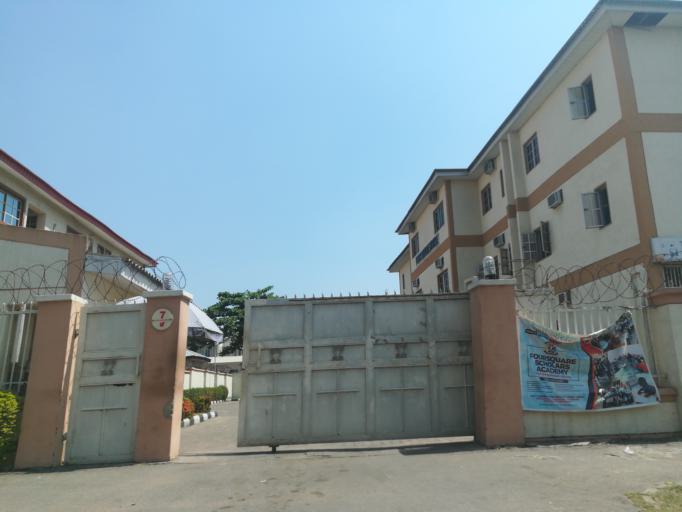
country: NG
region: Abuja Federal Capital Territory
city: Abuja
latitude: 9.0697
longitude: 7.4491
